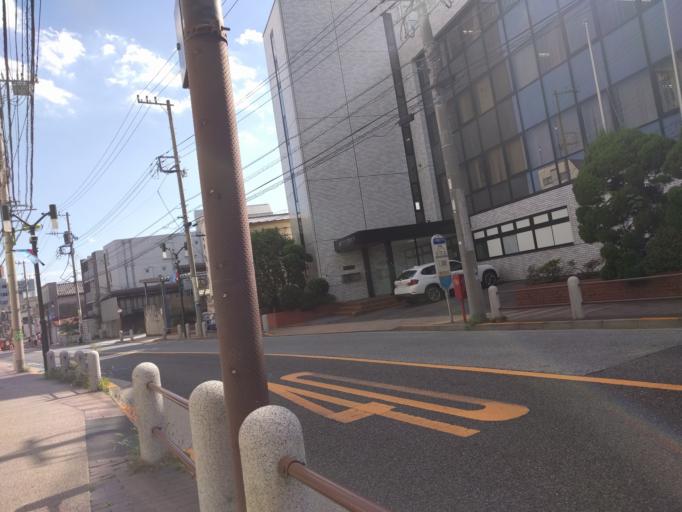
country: JP
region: Tokyo
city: Tokyo
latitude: 35.6305
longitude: 139.6336
